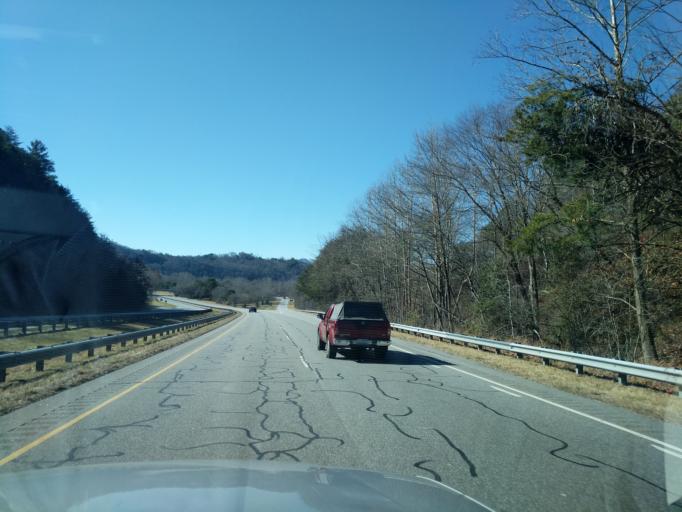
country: US
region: North Carolina
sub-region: Swain County
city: Bryson City
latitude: 35.4351
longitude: -83.3919
